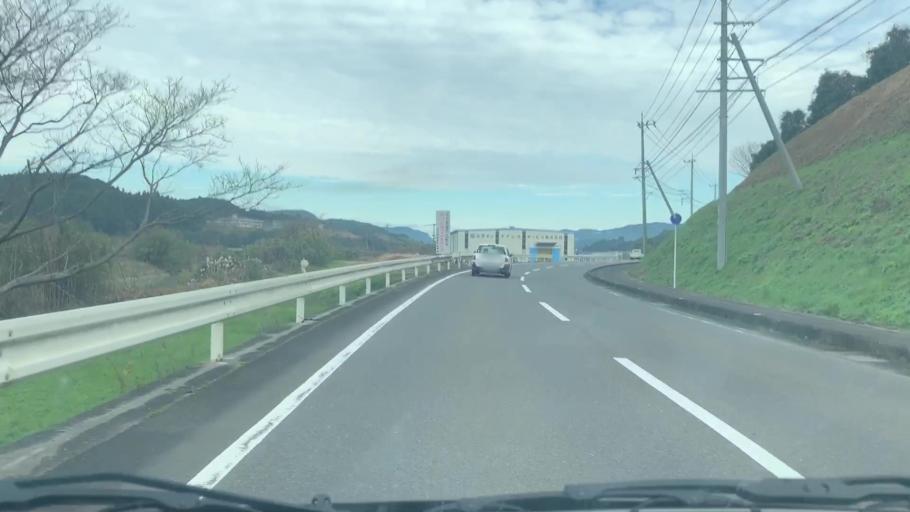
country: JP
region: Saga Prefecture
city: Imaricho-ko
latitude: 33.2779
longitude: 129.9653
